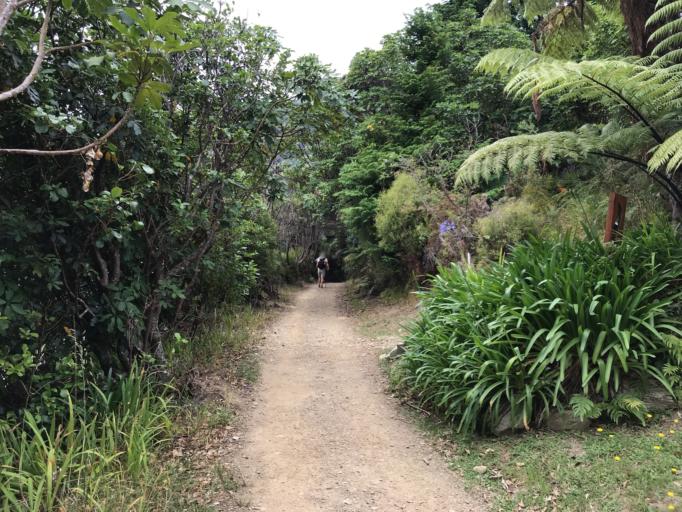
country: NZ
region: Marlborough
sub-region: Marlborough District
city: Picton
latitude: -41.1002
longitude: 174.1848
